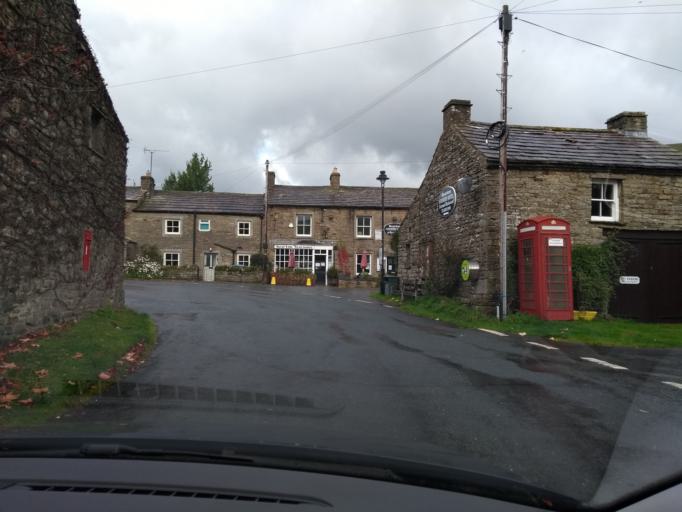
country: GB
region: England
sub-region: Cumbria
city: Kirkby Stephen
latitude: 54.3790
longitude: -2.1679
